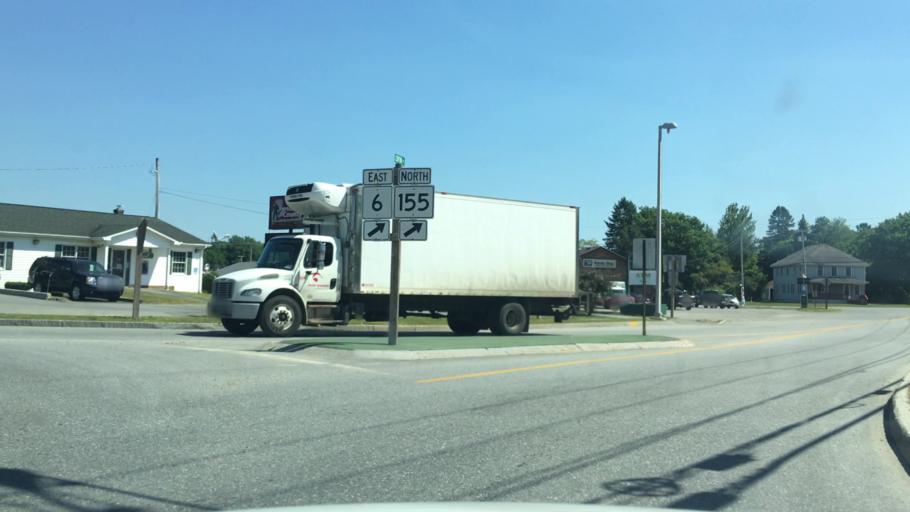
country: US
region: Maine
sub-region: Penobscot County
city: Howland
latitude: 45.2381
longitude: -68.6611
